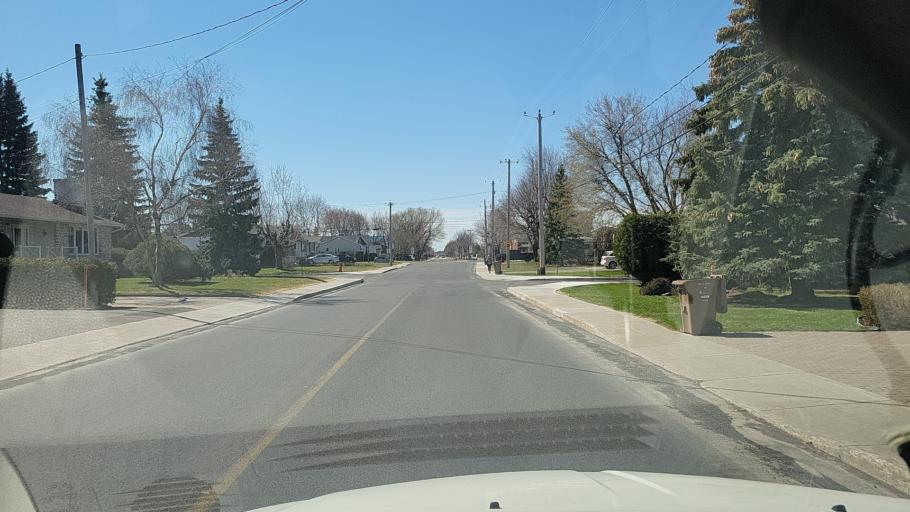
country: CA
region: Quebec
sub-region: Monteregie
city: Sainte-Julie
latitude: 45.5896
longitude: -73.3450
